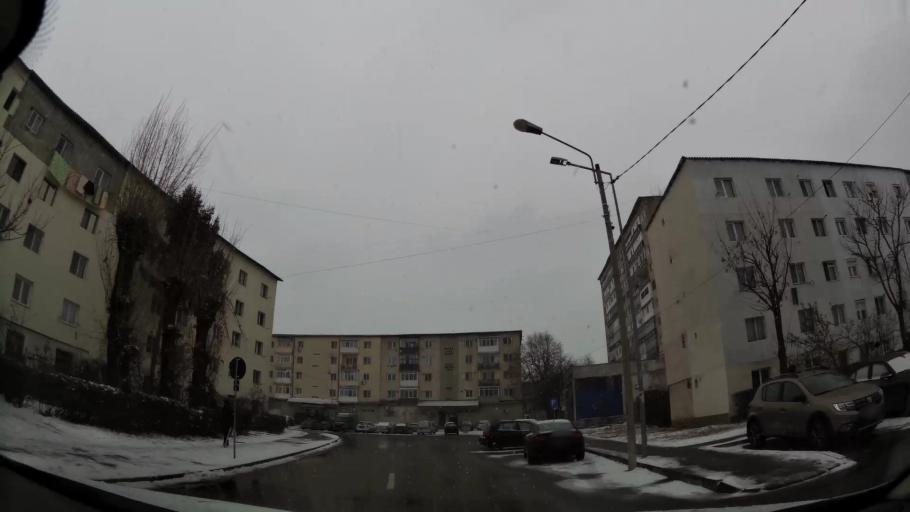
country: RO
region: Dambovita
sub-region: Municipiul Targoviste
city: Targoviste
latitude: 44.9228
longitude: 25.4474
